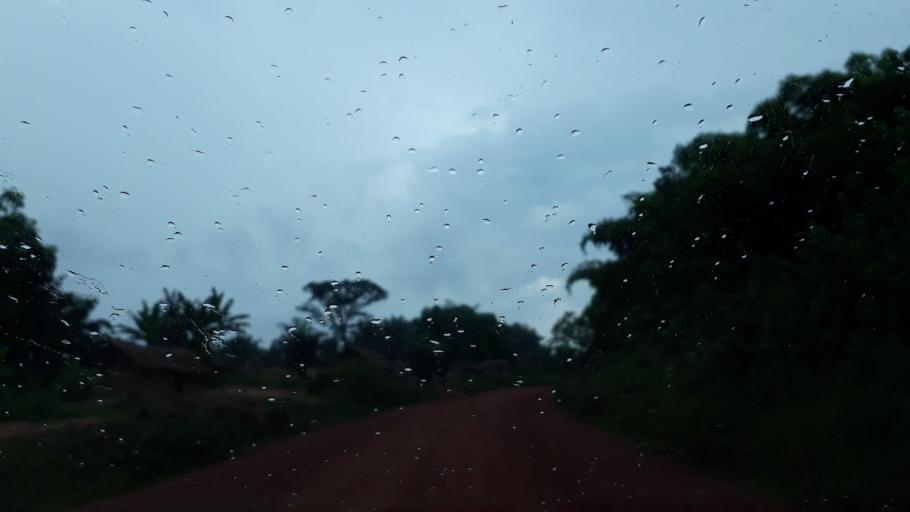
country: CD
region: Eastern Province
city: Kisangani
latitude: 0.4724
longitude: 25.4772
